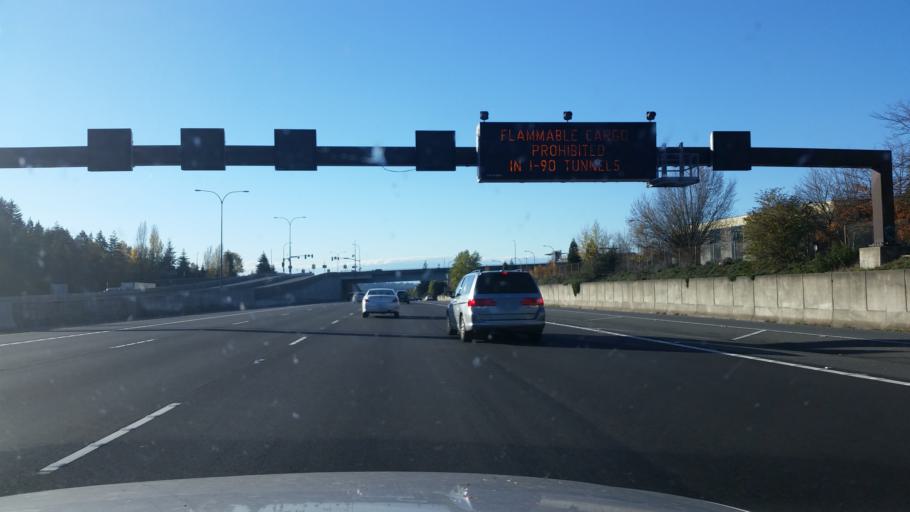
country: US
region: Washington
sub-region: King County
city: Eastgate
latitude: 47.5795
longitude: -122.1472
